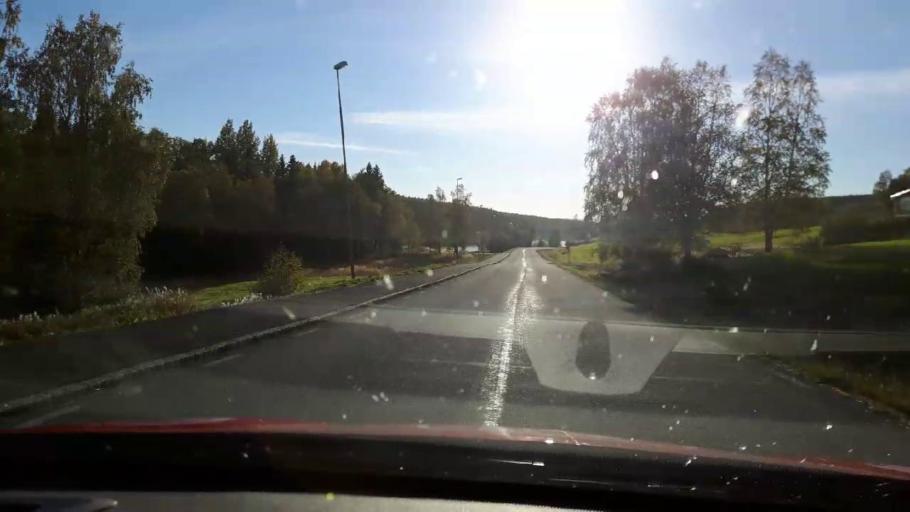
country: SE
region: Jaemtland
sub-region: OEstersunds Kommun
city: Lit
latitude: 63.8101
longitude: 14.7877
